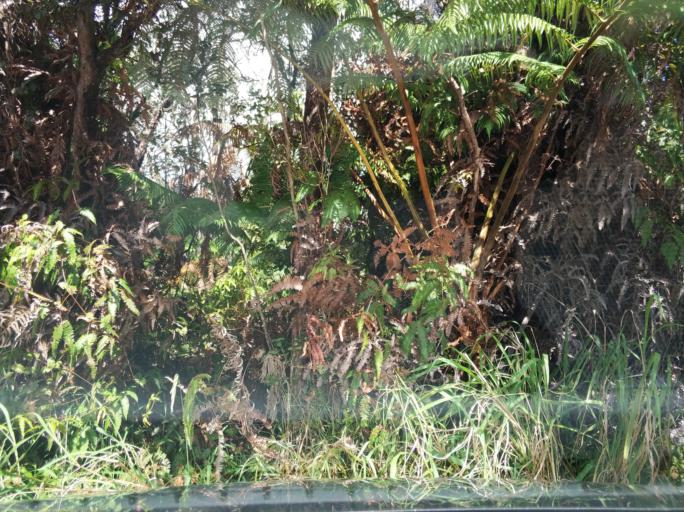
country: US
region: Hawaii
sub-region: Hawaii County
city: Volcano
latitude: 19.4164
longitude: -155.2426
